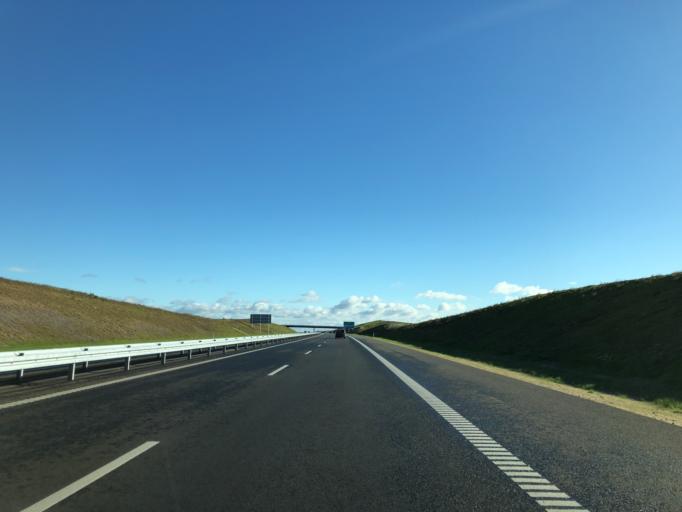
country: DK
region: Central Jutland
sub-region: Holstebro Kommune
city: Holstebro
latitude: 56.3825
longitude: 8.6671
